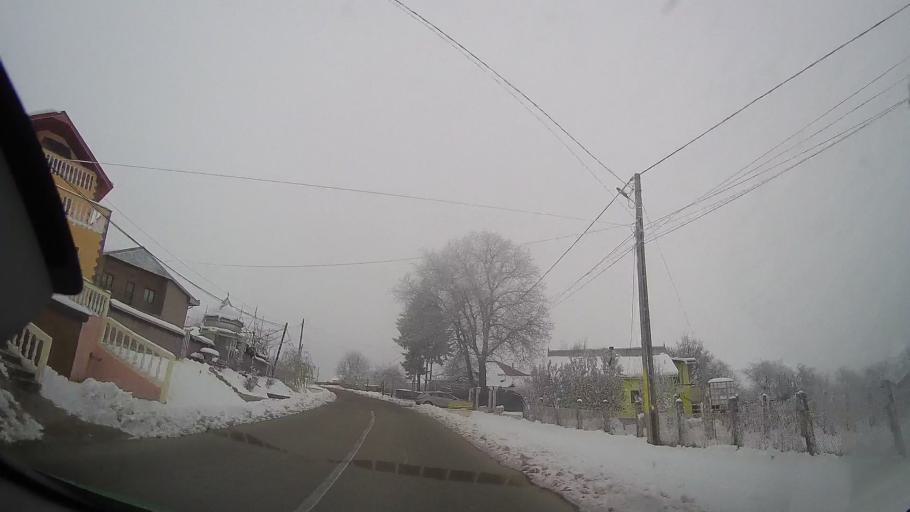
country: RO
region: Neamt
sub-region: Comuna Icusesti
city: Balusesti
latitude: 46.8642
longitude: 27.0031
